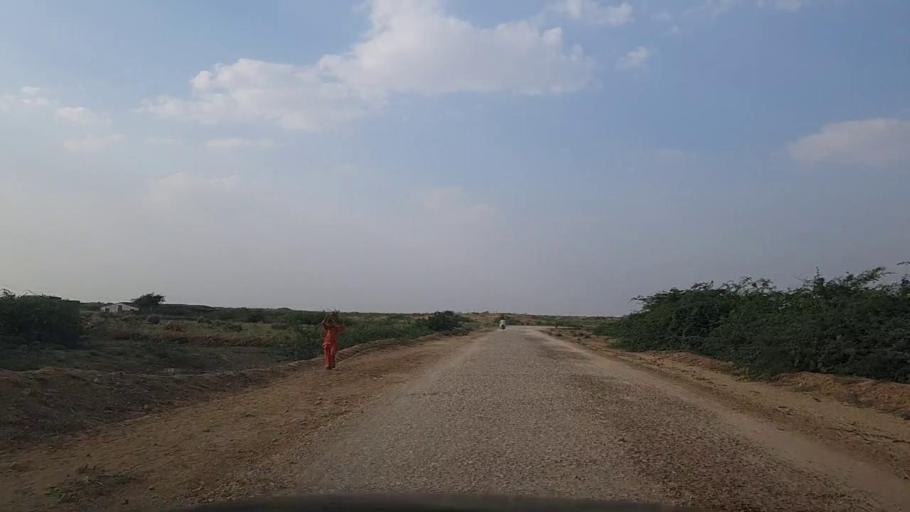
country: PK
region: Sindh
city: Gharo
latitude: 24.8049
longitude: 67.7415
